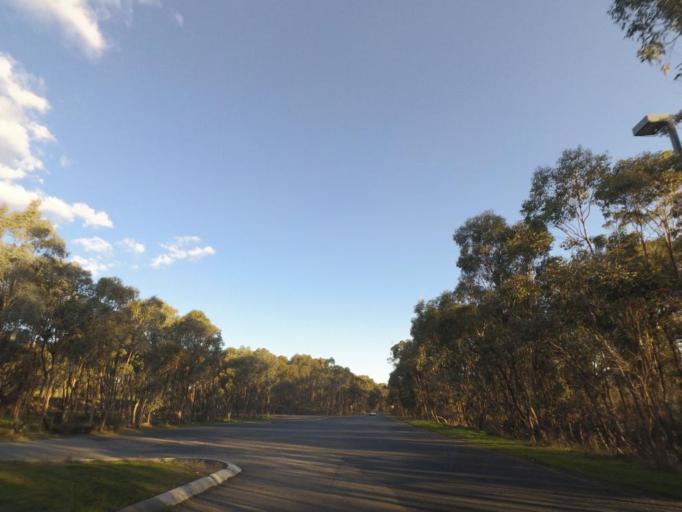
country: AU
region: Victoria
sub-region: Murrindindi
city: Kinglake West
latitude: -37.0642
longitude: 145.1019
